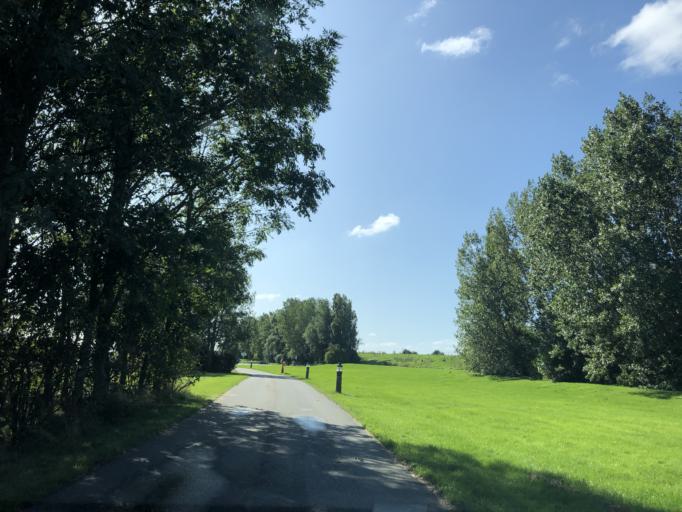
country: SE
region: Vaestra Goetaland
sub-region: Goteborg
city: Torslanda
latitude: 57.6957
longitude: 11.8139
